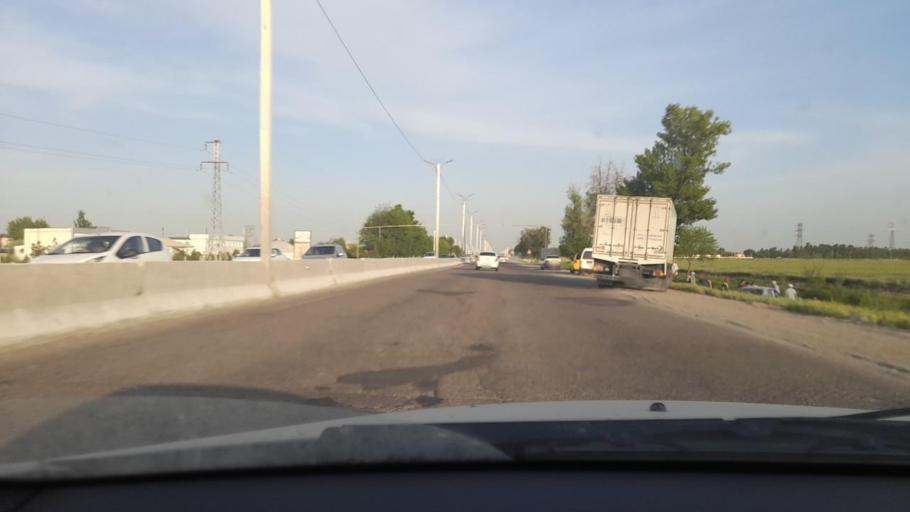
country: KZ
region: Ongtustik Qazaqstan
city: Myrzakent
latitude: 40.5523
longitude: 68.3985
